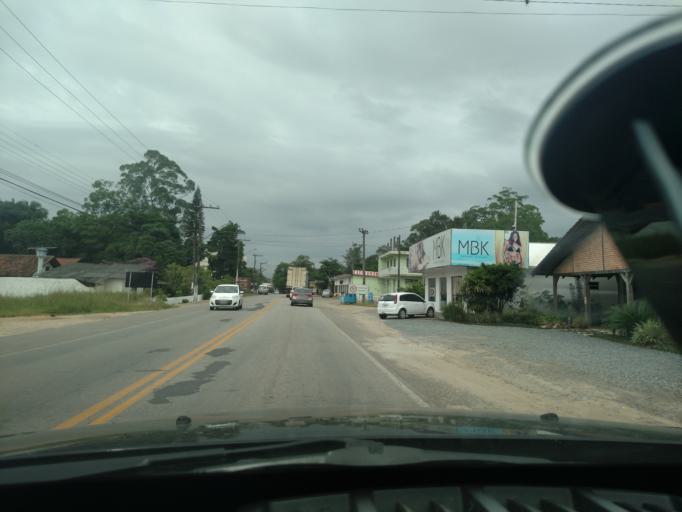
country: BR
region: Santa Catarina
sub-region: Gaspar
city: Gaspar
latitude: -26.8918
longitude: -48.8203
